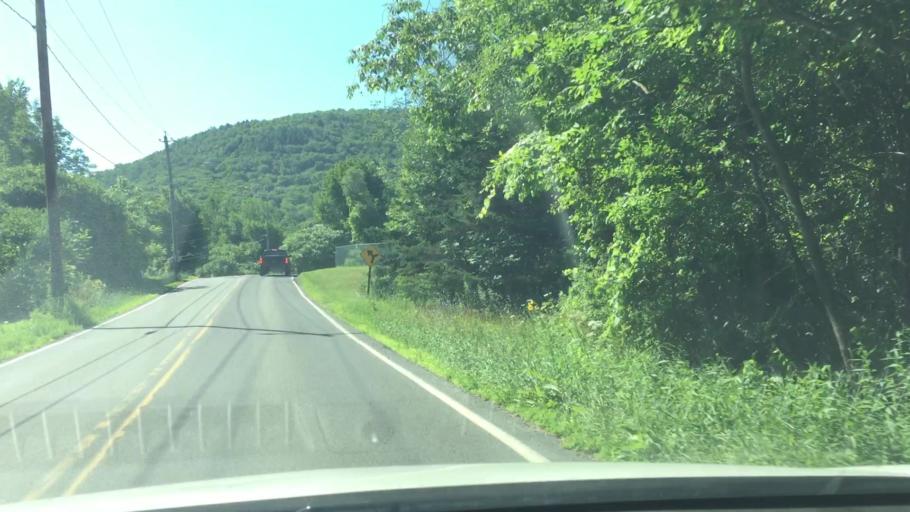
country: US
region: Massachusetts
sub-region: Berkshire County
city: Pittsfield
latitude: 42.4215
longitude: -73.2924
